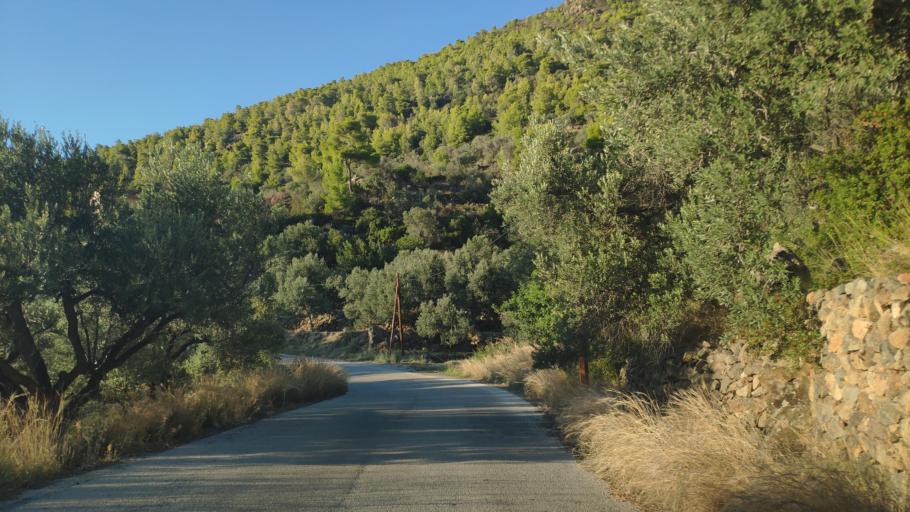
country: GR
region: Attica
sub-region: Nomos Piraios
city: Megalochori
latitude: 37.5995
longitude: 23.3371
